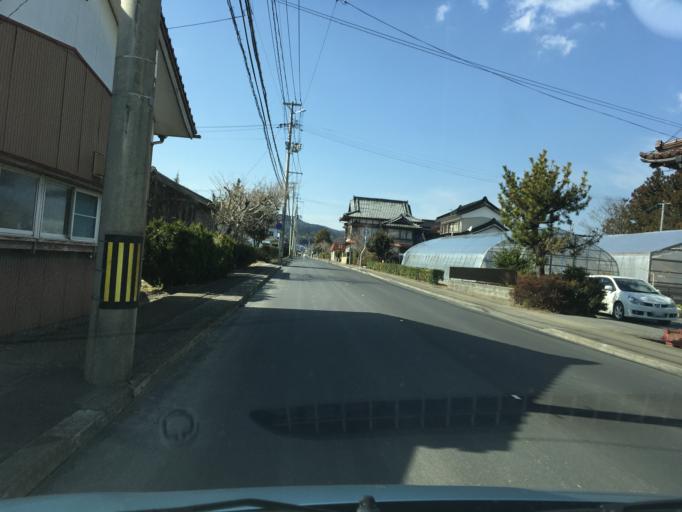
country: JP
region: Iwate
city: Ofunato
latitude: 38.8332
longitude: 141.5830
